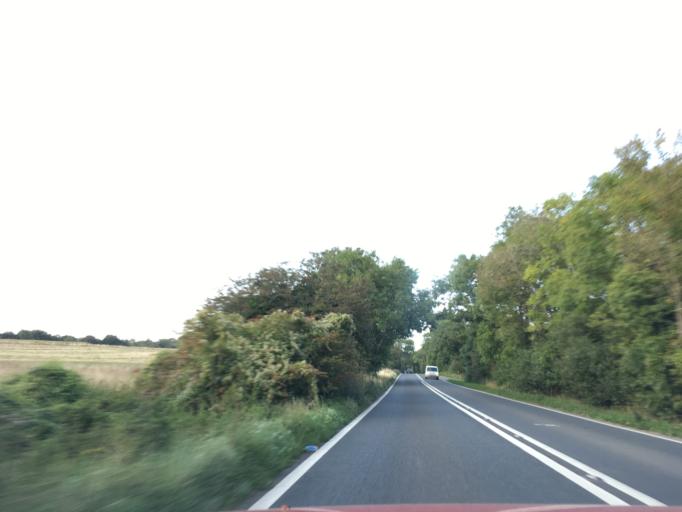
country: GB
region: England
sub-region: Gloucestershire
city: Northleach
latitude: 51.8611
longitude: -1.7998
